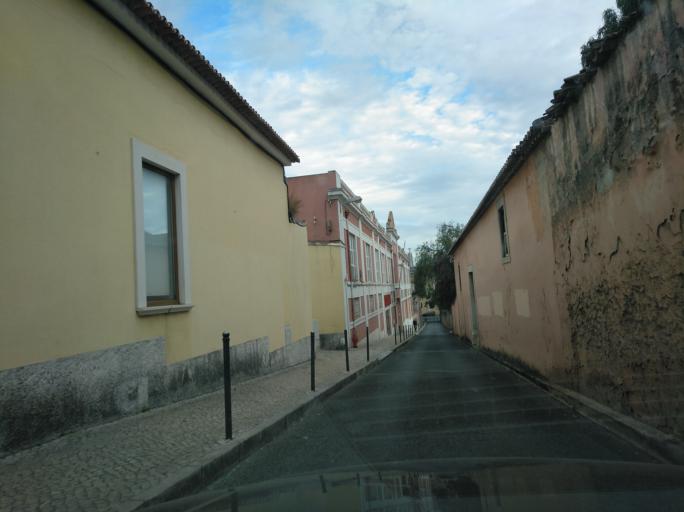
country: PT
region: Setubal
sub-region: Almada
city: Pragal
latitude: 38.6996
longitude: -9.1901
